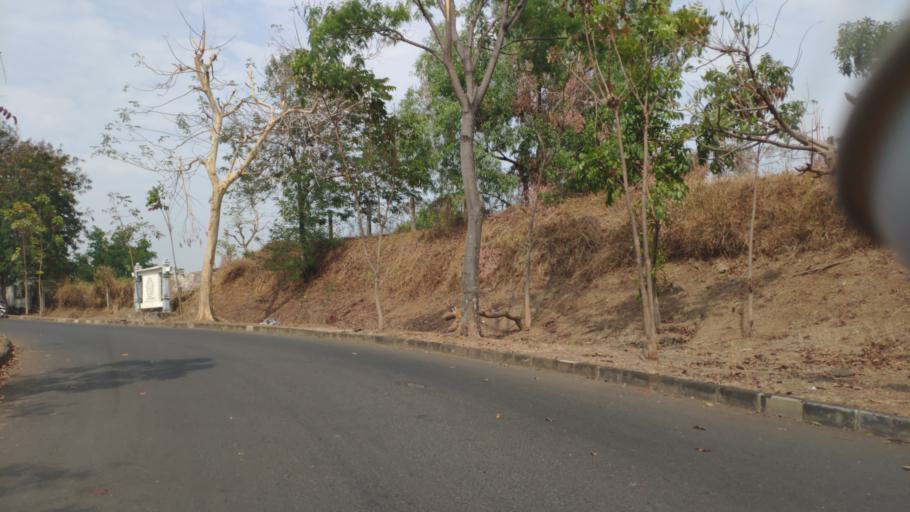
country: ID
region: Central Java
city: Semarang
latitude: -7.0470
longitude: 110.4353
